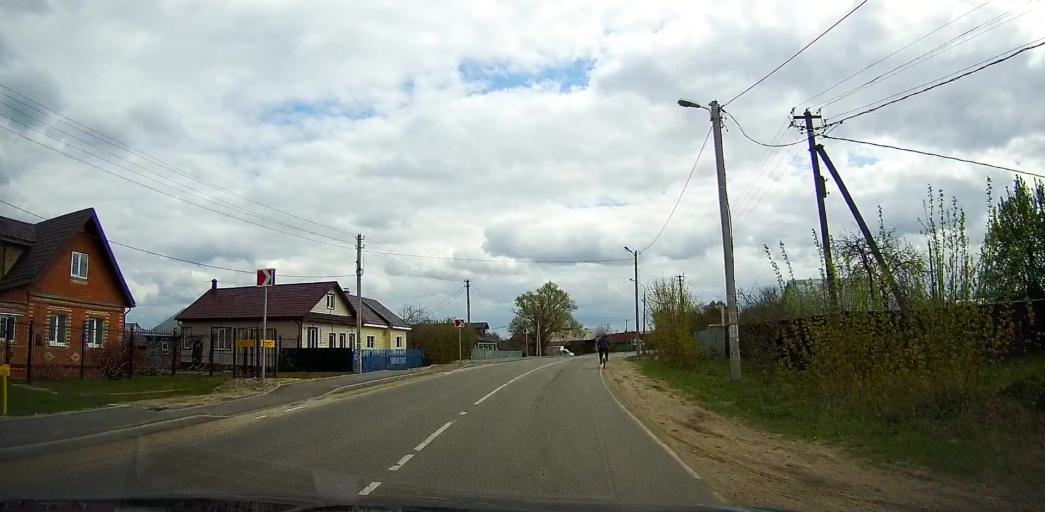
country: RU
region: Moskovskaya
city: Imeni Tsyurupy
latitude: 55.4976
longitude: 38.6513
